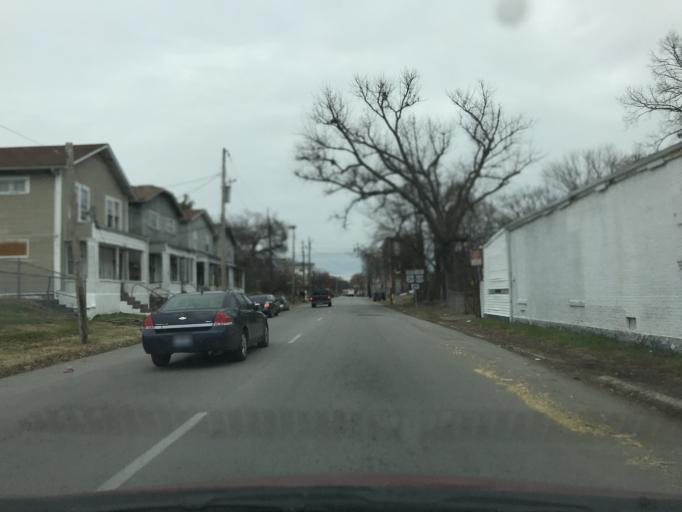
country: US
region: Kentucky
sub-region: Jefferson County
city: Louisville
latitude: 38.2571
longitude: -85.7851
